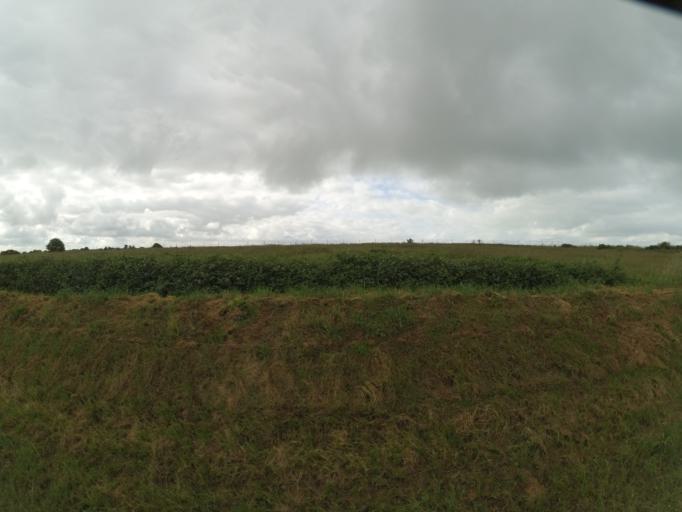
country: FR
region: Poitou-Charentes
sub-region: Departement de la Charente-Maritime
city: Aytre
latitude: 46.1314
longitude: -1.1446
